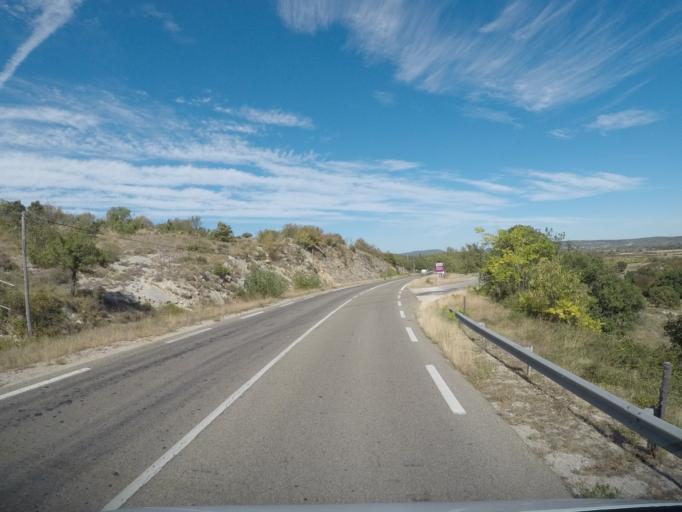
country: FR
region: Languedoc-Roussillon
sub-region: Departement de l'Herault
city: Saint-Martin-de-Londres
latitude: 43.8048
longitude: 3.7384
